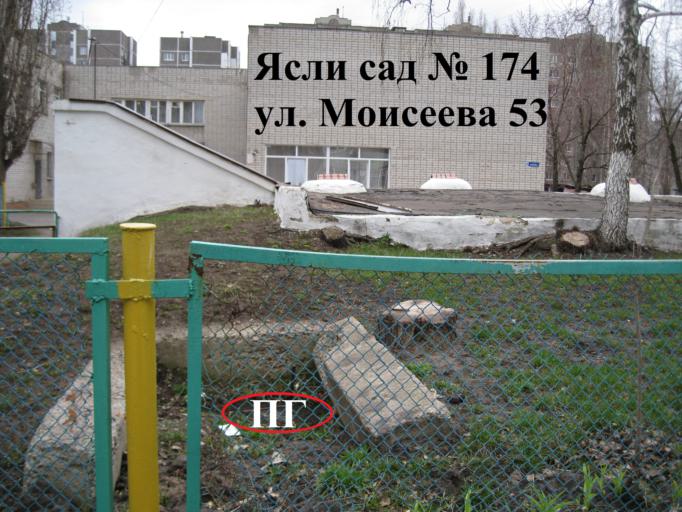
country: RU
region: Voronezj
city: Voronezh
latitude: 51.6507
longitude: 39.1783
